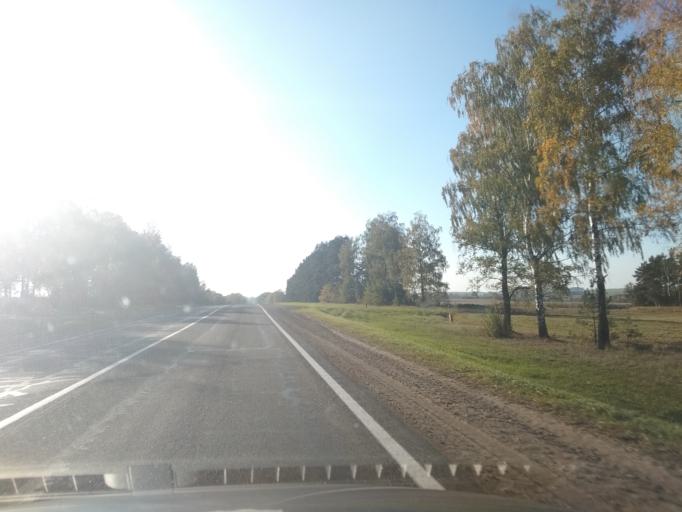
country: BY
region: Grodnenskaya
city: Svislach
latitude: 53.1259
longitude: 24.1232
